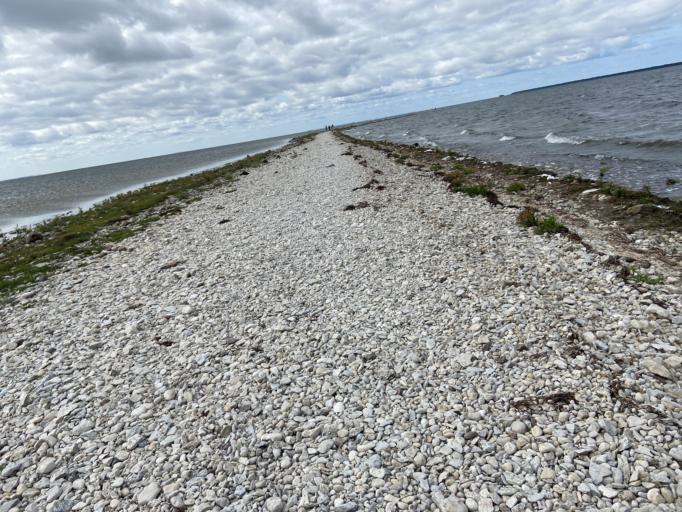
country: EE
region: Hiiumaa
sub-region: Kaerdla linn
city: Kardla
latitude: 58.7575
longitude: 22.7924
